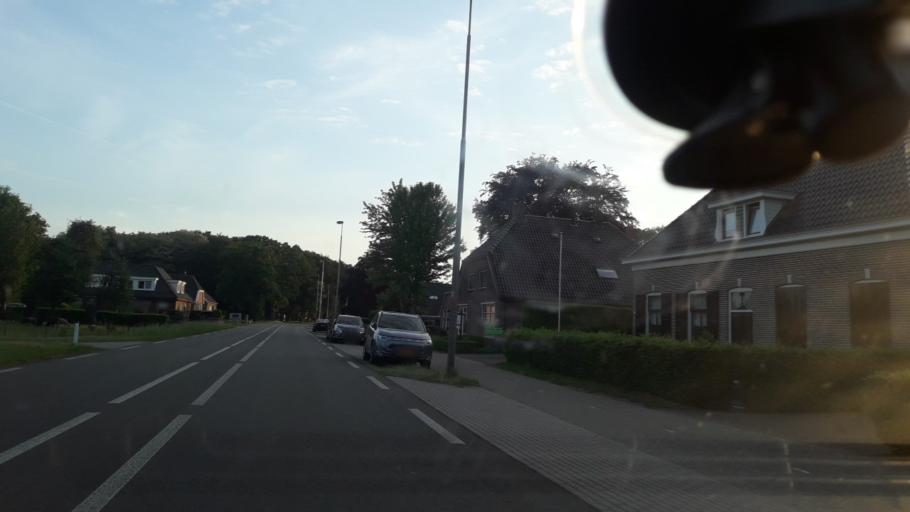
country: NL
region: Gelderland
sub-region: Gemeente Oldebroek
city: Oldebroek
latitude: 52.4552
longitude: 5.9270
